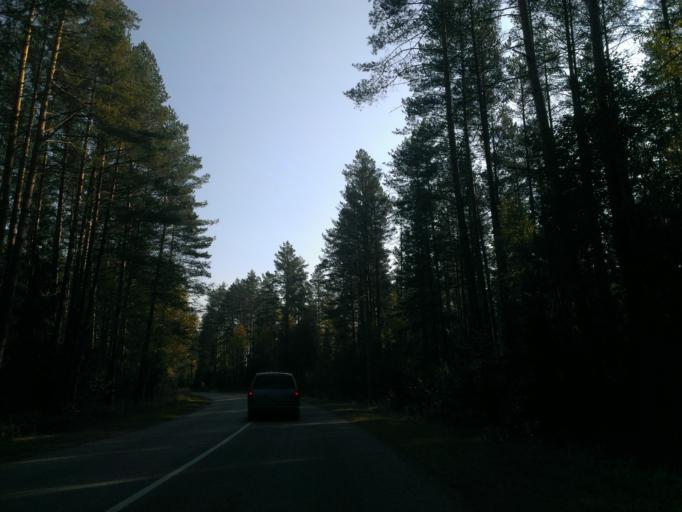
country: LV
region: Garkalne
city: Garkalne
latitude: 57.0162
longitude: 24.4432
